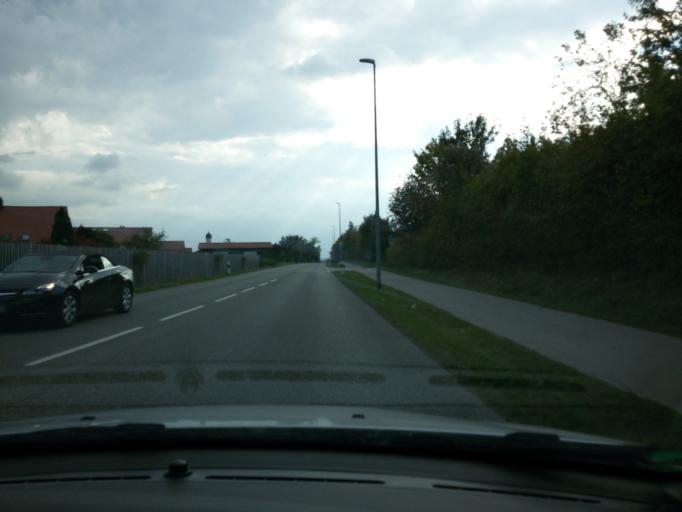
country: DE
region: Bavaria
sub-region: Swabia
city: Buchloe
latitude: 48.0223
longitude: 10.7158
